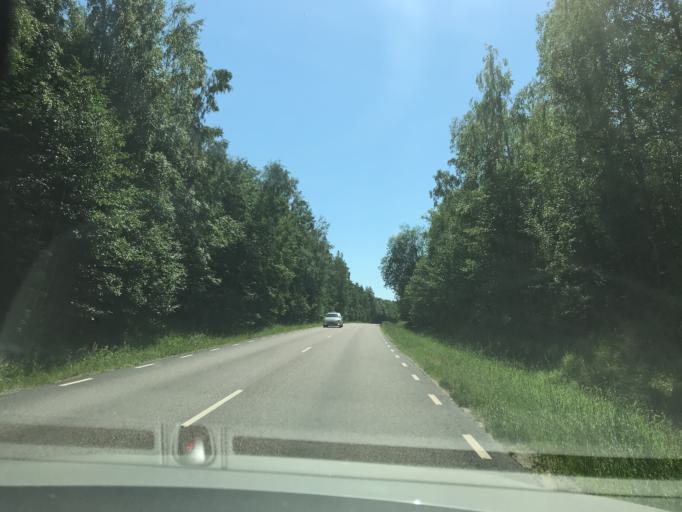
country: SE
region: Vaestra Goetaland
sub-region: Gotene Kommun
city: Goetene
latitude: 58.6097
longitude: 13.4009
